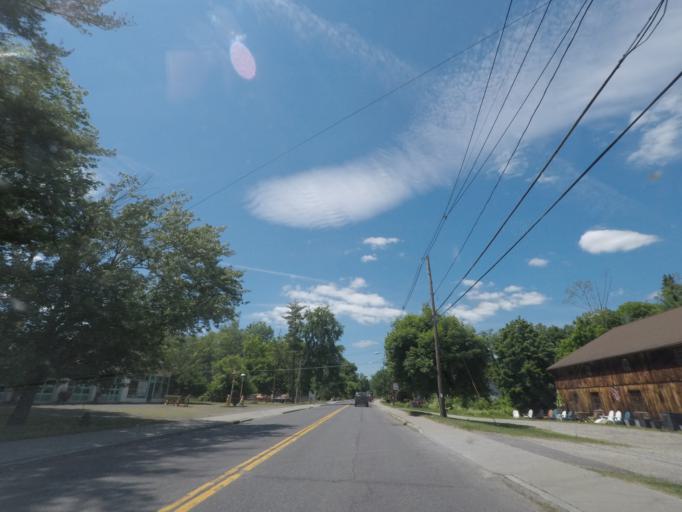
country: US
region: New York
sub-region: Dutchess County
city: Pine Plains
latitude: 41.9542
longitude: -73.5138
